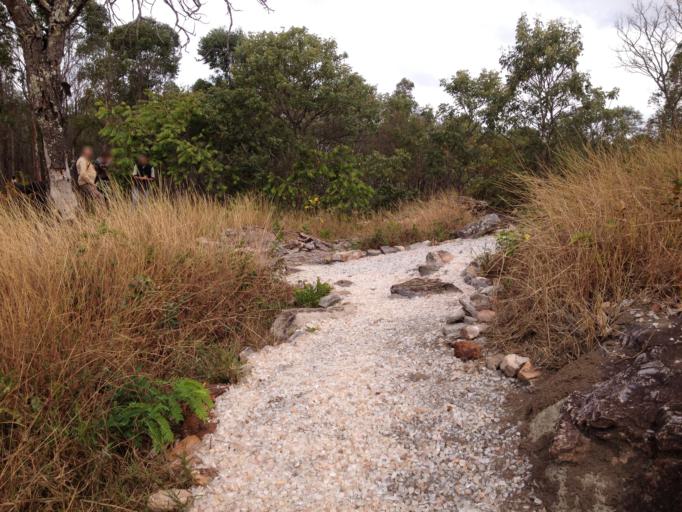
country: BR
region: Goias
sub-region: Cristalina
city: Cristalina
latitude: -16.7307
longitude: -47.5548
